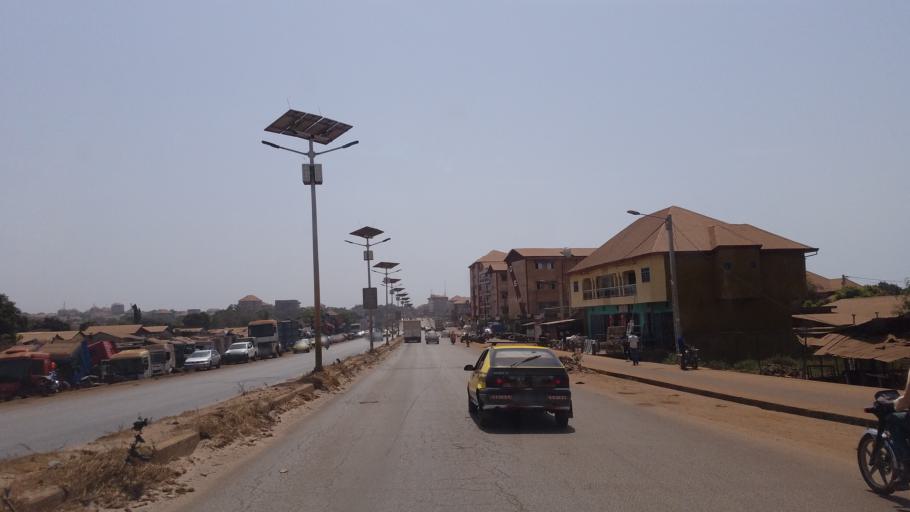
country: GN
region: Conakry
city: Conakry
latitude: 9.6518
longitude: -13.5795
